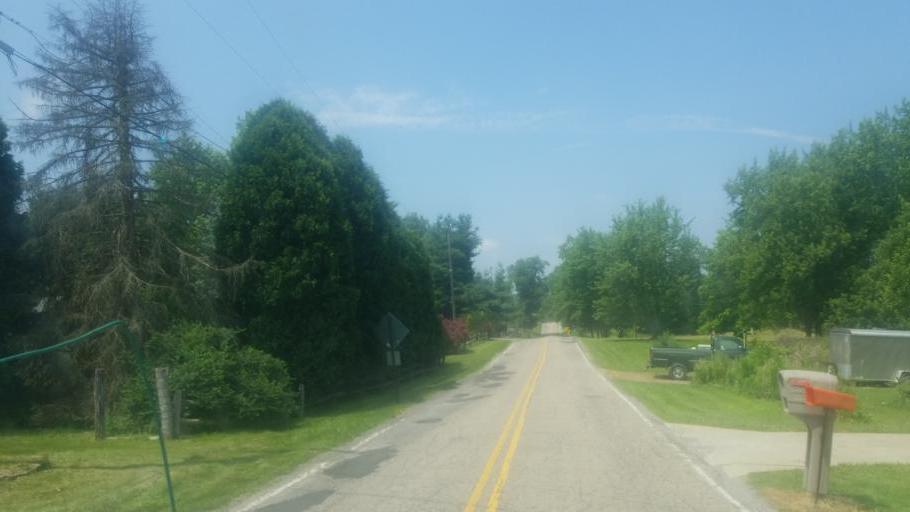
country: US
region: Ohio
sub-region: Columbiana County
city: Columbiana
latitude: 40.9204
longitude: -80.6893
